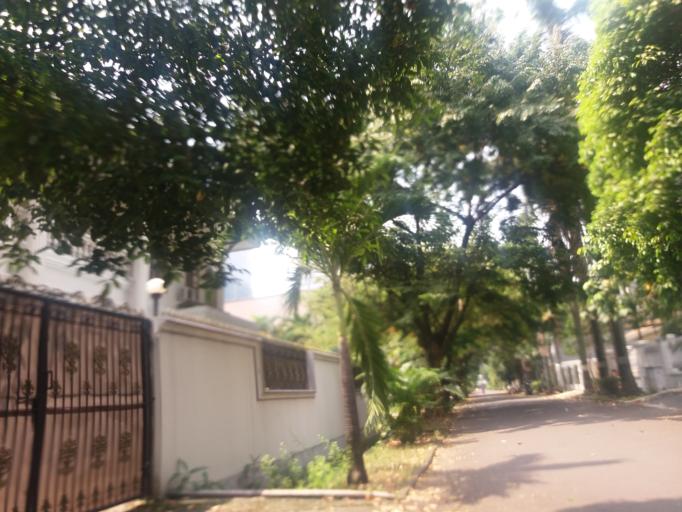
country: ID
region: Jakarta Raya
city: Jakarta
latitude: -6.2280
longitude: 106.8292
